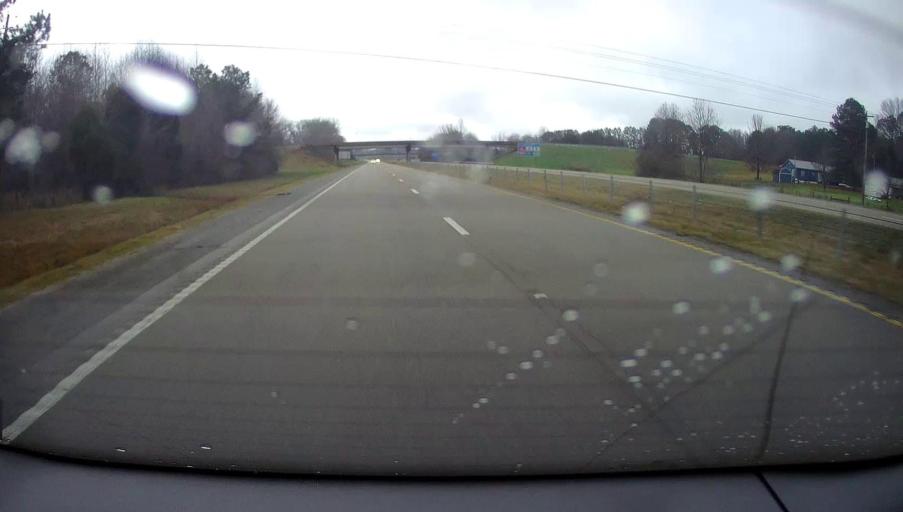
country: US
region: Mississippi
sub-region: Alcorn County
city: Corinth
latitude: 34.9226
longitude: -88.5435
